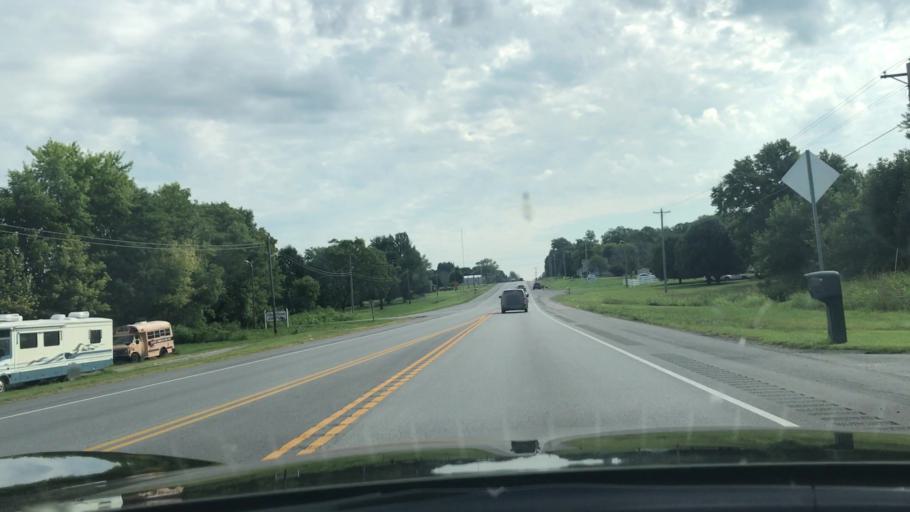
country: US
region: Kentucky
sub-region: Taylor County
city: Campbellsville
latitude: 37.3280
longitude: -85.3889
